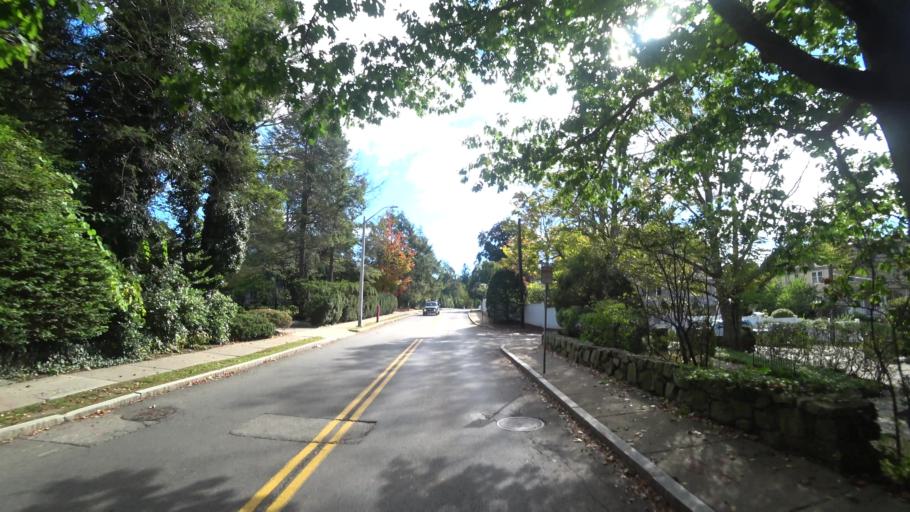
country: US
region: Massachusetts
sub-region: Middlesex County
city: Newton
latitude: 42.3304
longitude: -71.1688
